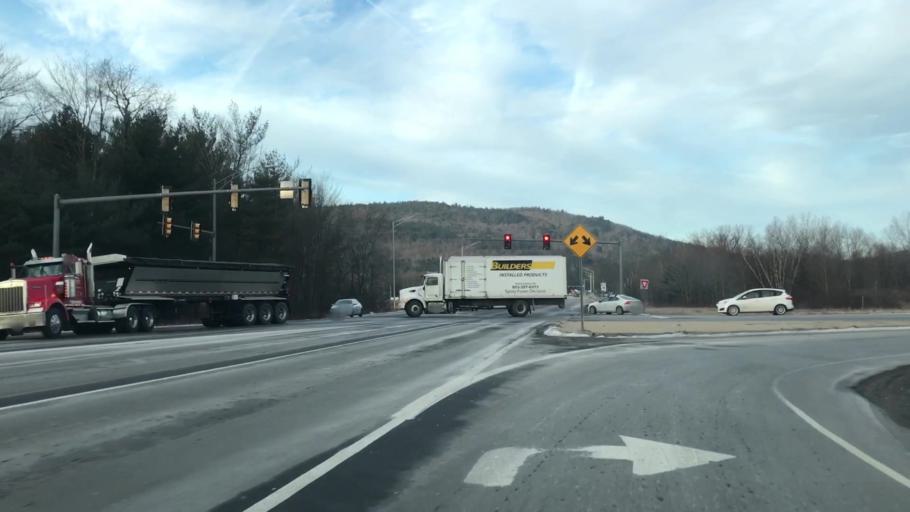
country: US
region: New Hampshire
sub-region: Cheshire County
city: Keene
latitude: 42.9228
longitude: -72.3003
